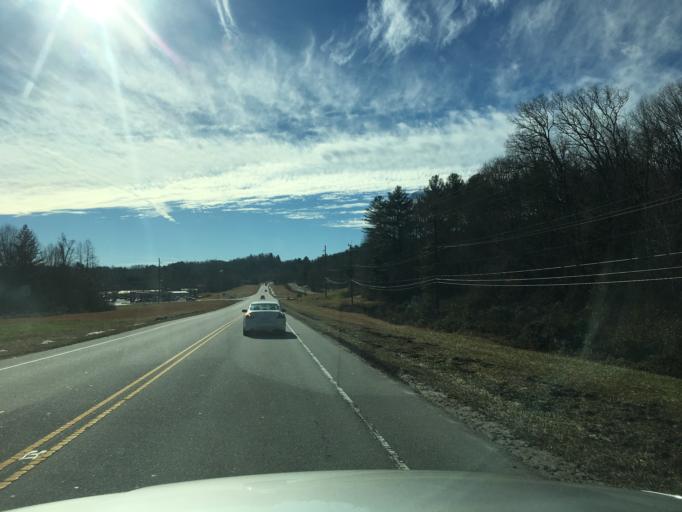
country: US
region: North Carolina
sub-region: Transylvania County
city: Brevard
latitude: 35.1729
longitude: -82.8052
